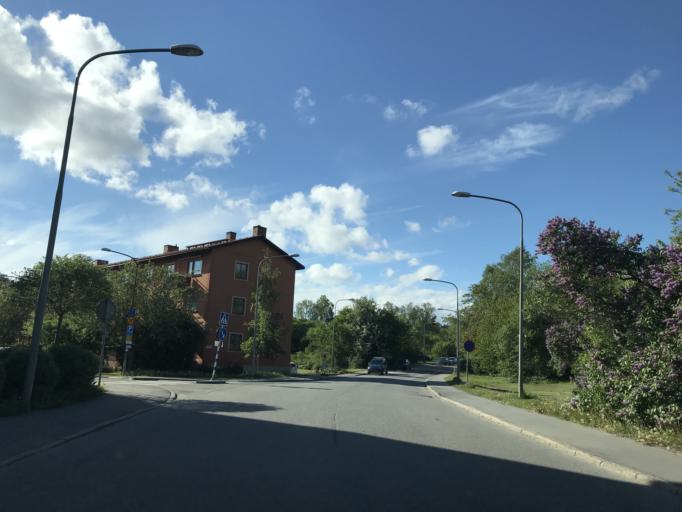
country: SE
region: Stockholm
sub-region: Stockholms Kommun
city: Bromma
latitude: 59.3402
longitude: 17.9512
